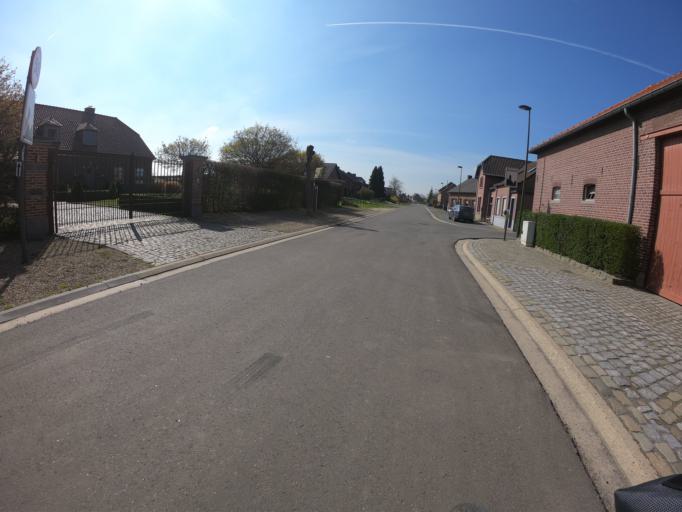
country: BE
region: Flanders
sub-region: Provincie Limburg
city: Nieuwerkerken
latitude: 50.8942
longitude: 5.1671
